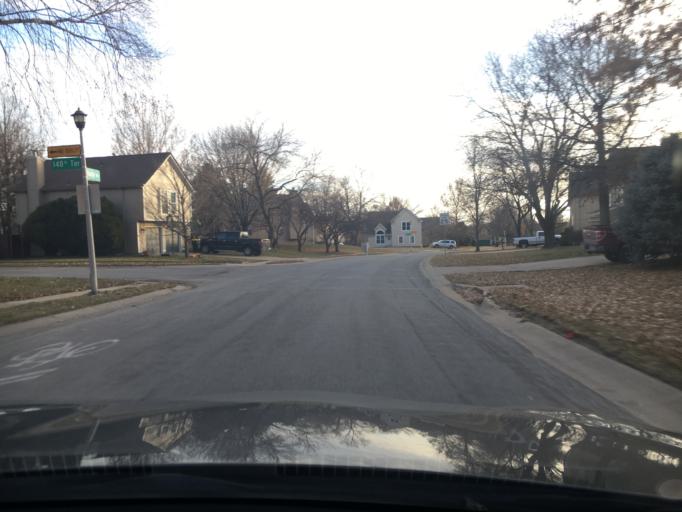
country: US
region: Kansas
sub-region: Johnson County
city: Lenexa
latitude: 38.8592
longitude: -94.6801
